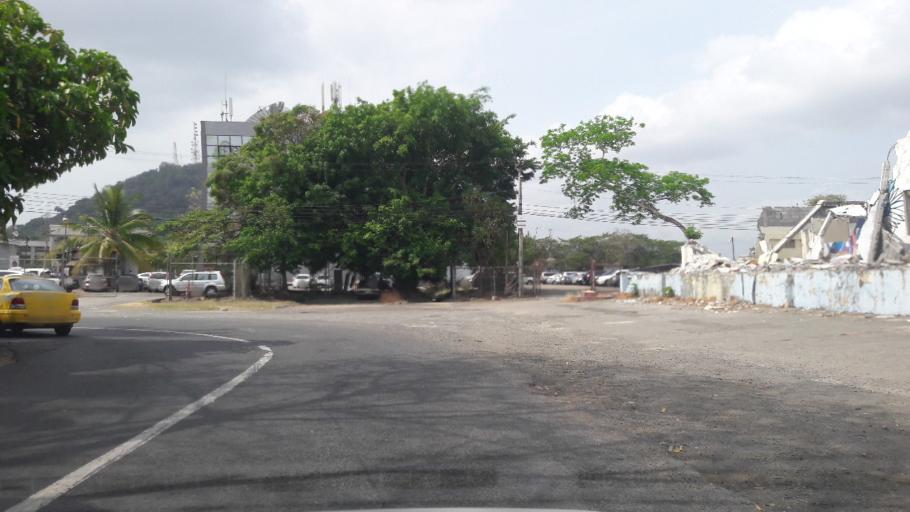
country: PA
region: Panama
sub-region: Distrito de Panama
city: Ancon
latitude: 8.9709
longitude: -79.5482
